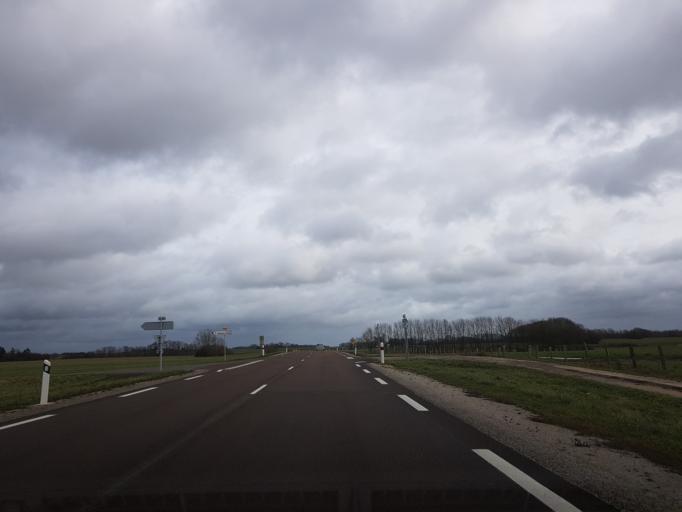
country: FR
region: Champagne-Ardenne
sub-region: Departement de la Haute-Marne
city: Chalindrey
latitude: 47.8460
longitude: 5.4424
